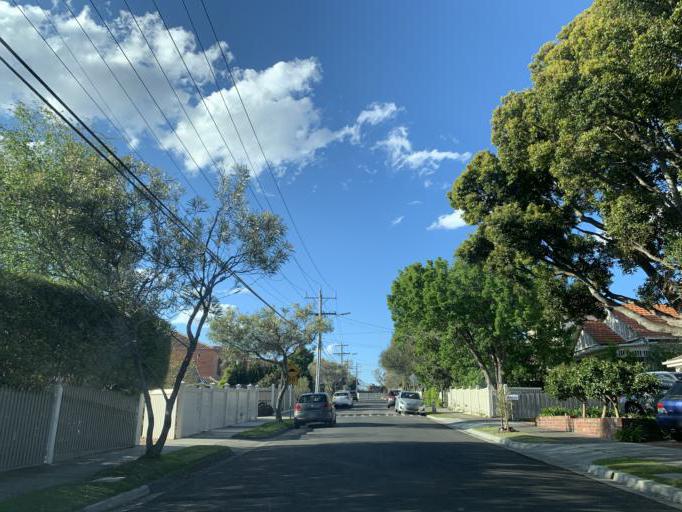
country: AU
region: Victoria
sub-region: Bayside
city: Hampton
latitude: -37.9390
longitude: 145.0118
